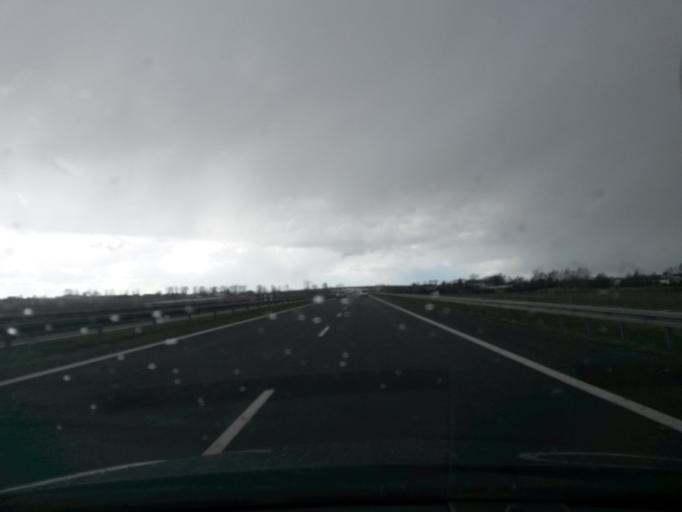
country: PL
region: Greater Poland Voivodeship
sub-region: Powiat poznanski
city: Kleszczewo
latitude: 52.3102
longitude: 17.2407
